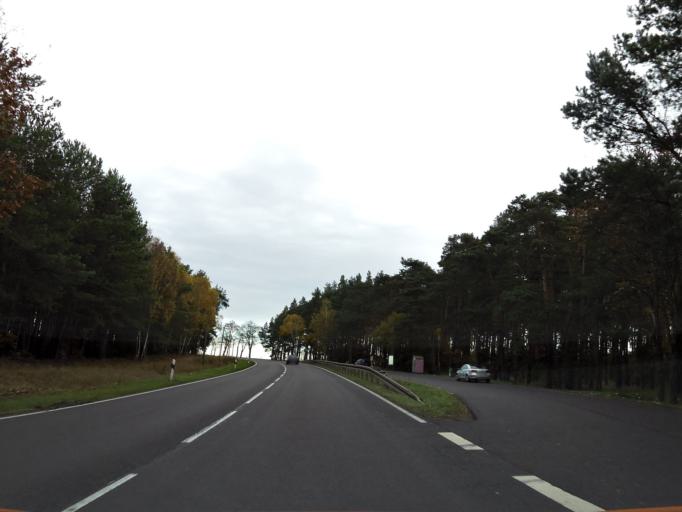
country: DE
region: Saxony-Anhalt
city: Letzlingen
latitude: 52.4254
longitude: 11.4837
